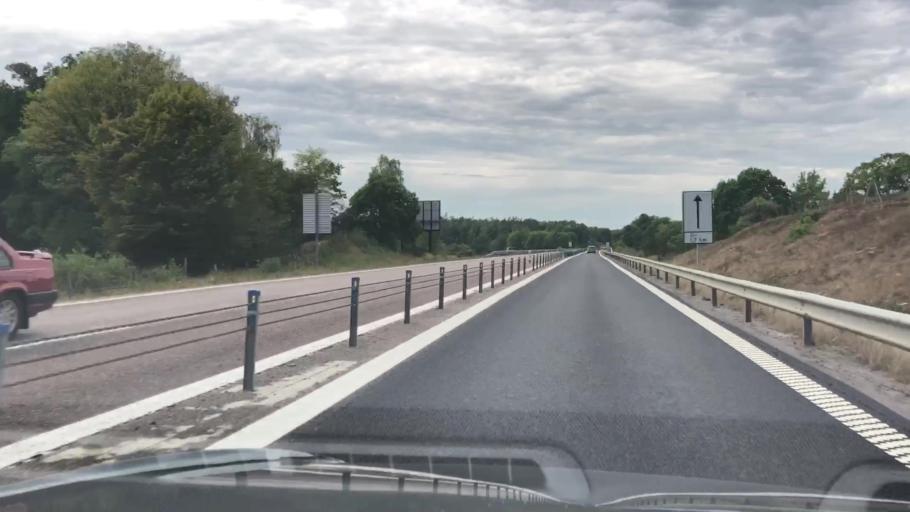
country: SE
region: Blekinge
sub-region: Ronneby Kommun
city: Brakne-Hoby
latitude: 56.2105
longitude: 15.0897
